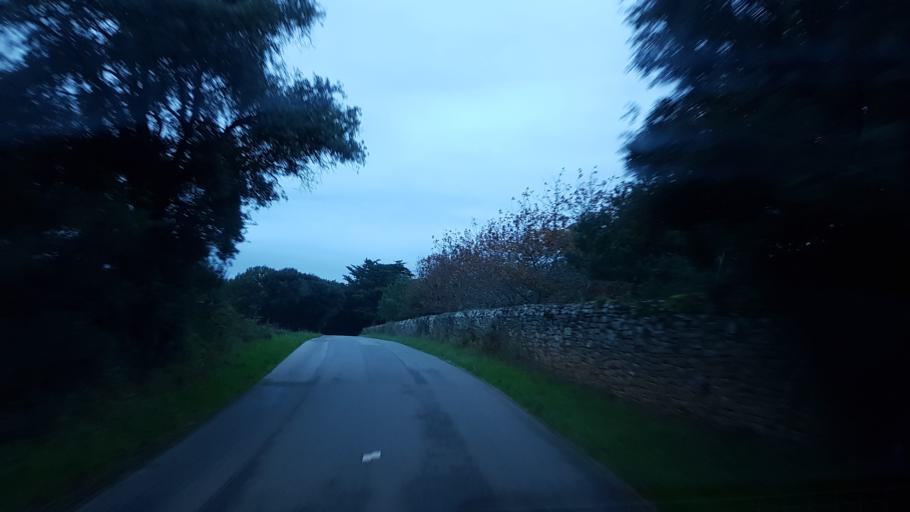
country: FR
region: Brittany
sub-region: Departement du Morbihan
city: Sarzeau
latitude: 47.5349
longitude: -2.7765
